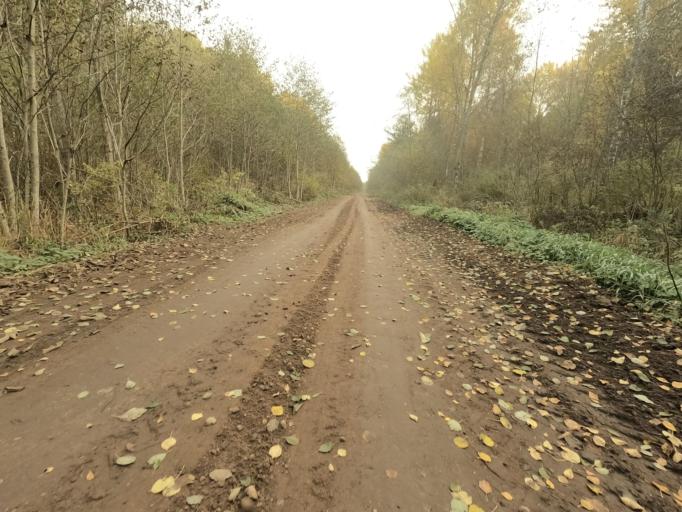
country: RU
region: Novgorod
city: Batetskiy
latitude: 58.8792
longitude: 30.7631
